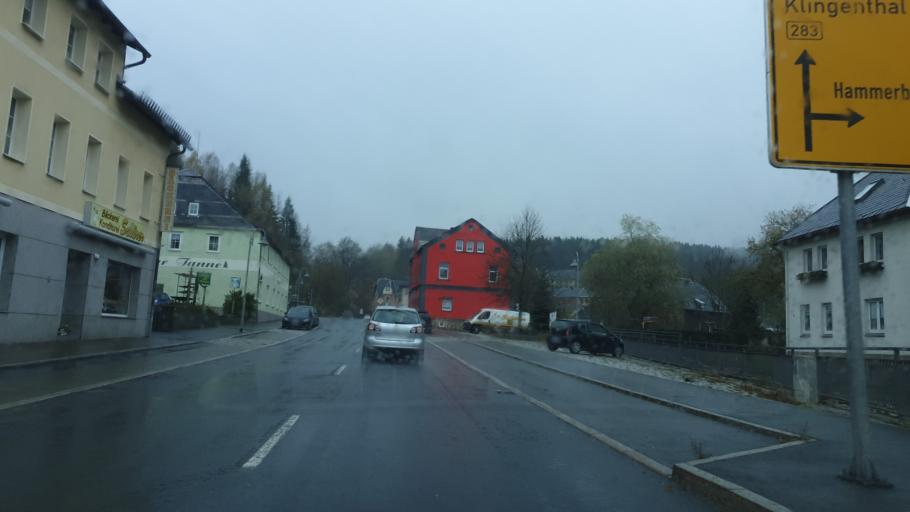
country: DE
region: Saxony
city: Tannenbergsthal
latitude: 50.4365
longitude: 12.4614
